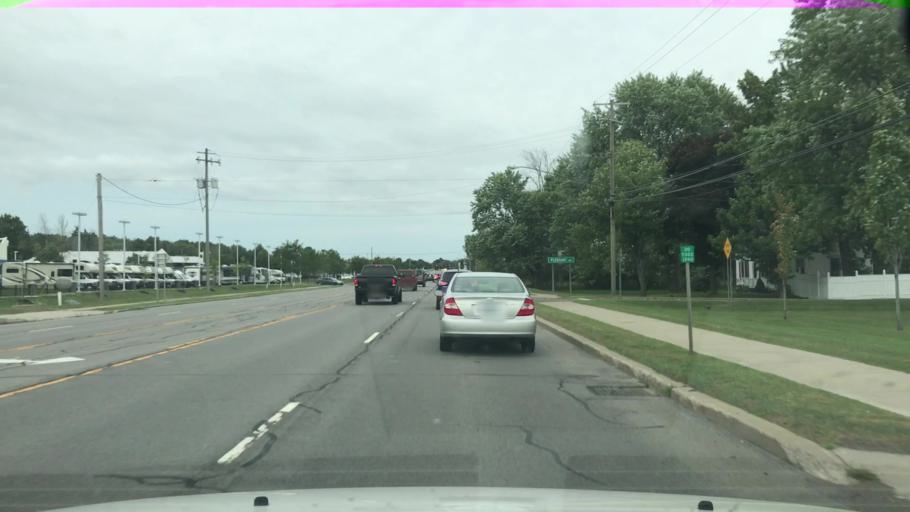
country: US
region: New York
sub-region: Erie County
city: Orchard Park
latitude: 42.7922
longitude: -78.7571
